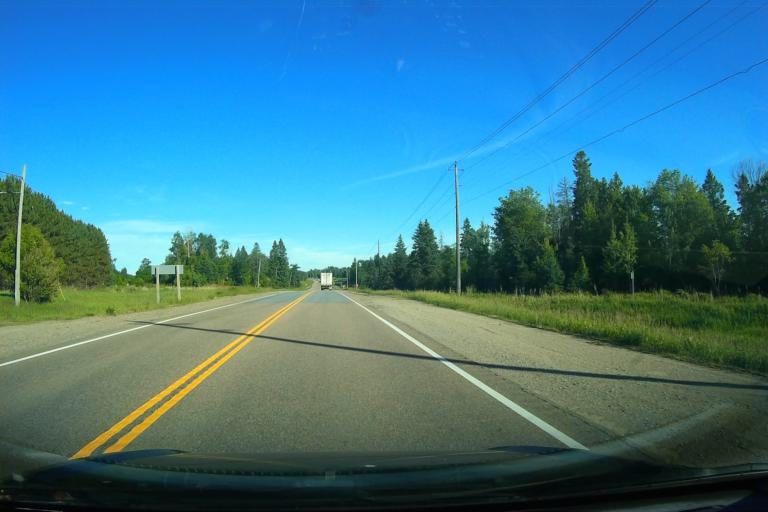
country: CA
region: Ontario
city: Renfrew
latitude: 45.5886
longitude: -76.8335
